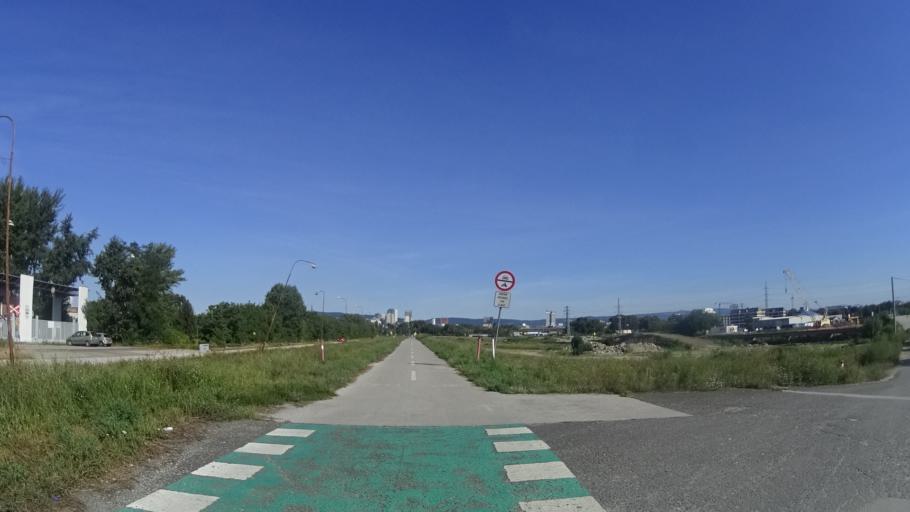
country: SK
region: Bratislavsky
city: Bratislava
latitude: 48.1336
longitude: 17.1549
